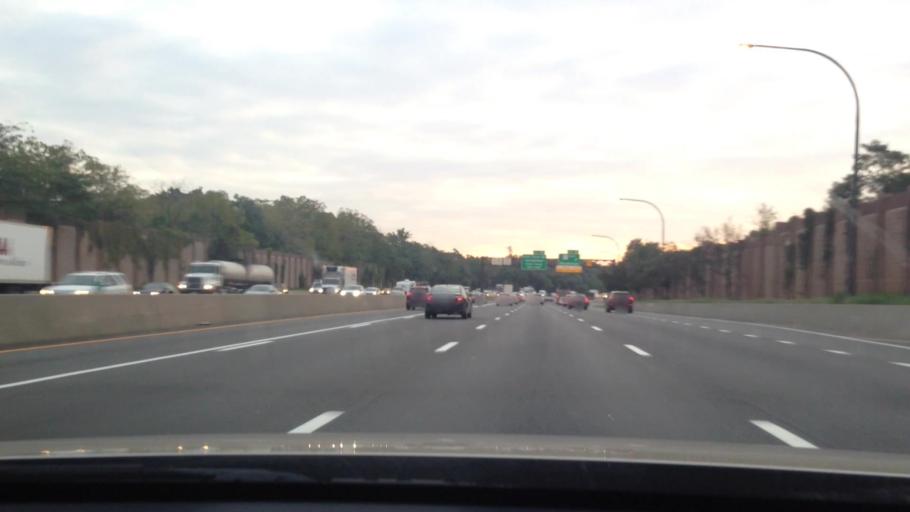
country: US
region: New York
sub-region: Nassau County
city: East Hills
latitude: 40.7855
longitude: -73.6325
